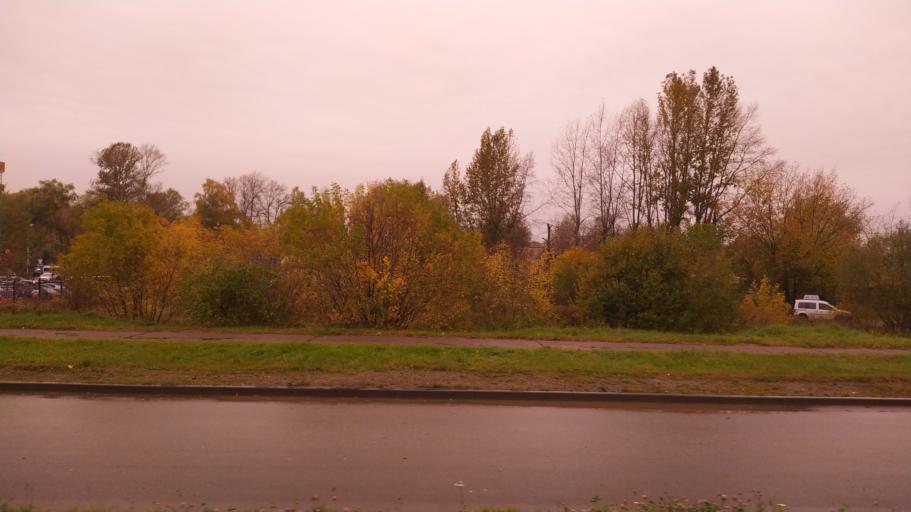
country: RU
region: Tverskaya
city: Tver
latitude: 56.8299
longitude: 35.8993
